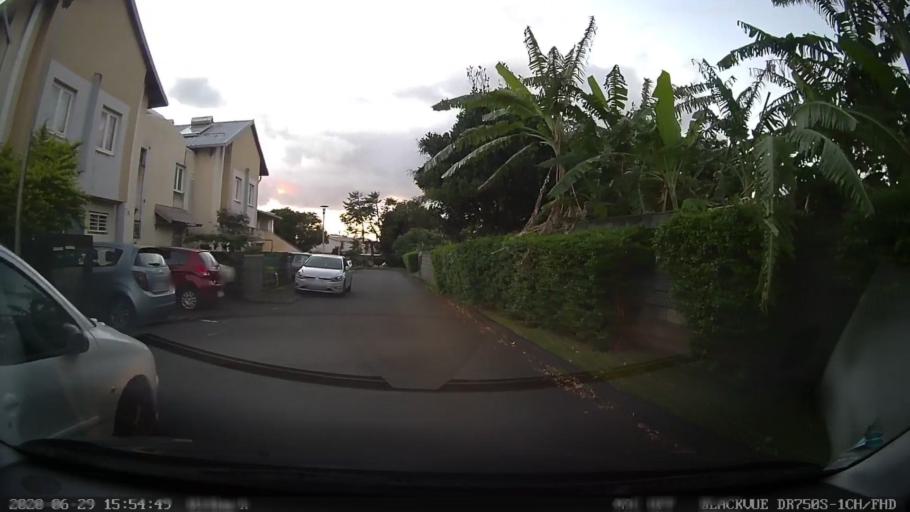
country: RE
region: Reunion
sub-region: Reunion
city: Bras-Panon
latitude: -21.0006
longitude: 55.6946
